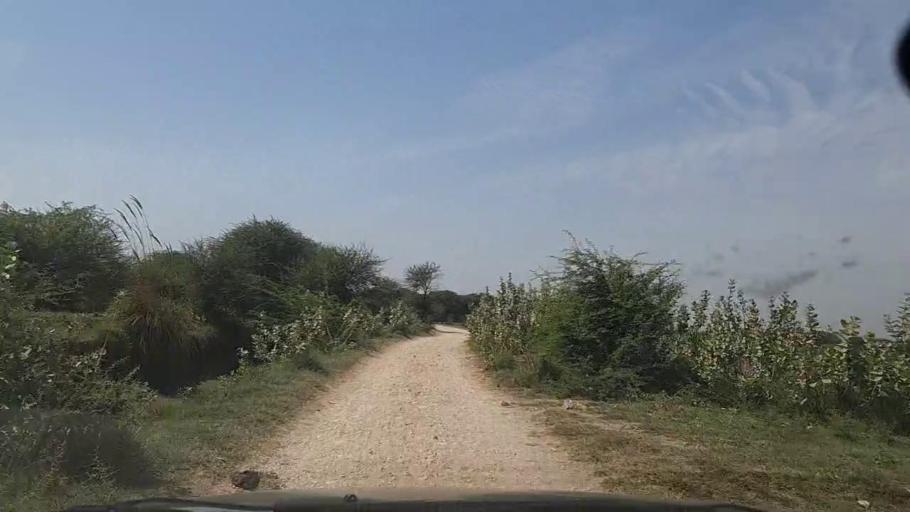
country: PK
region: Sindh
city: Mirpur Batoro
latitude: 24.6523
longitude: 68.1607
